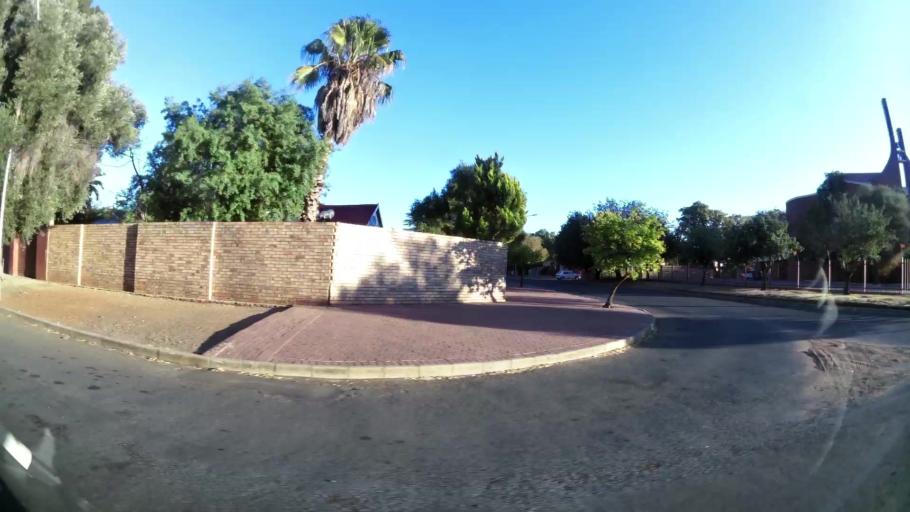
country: ZA
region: Northern Cape
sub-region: Frances Baard District Municipality
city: Kimberley
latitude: -28.7624
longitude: 24.7637
